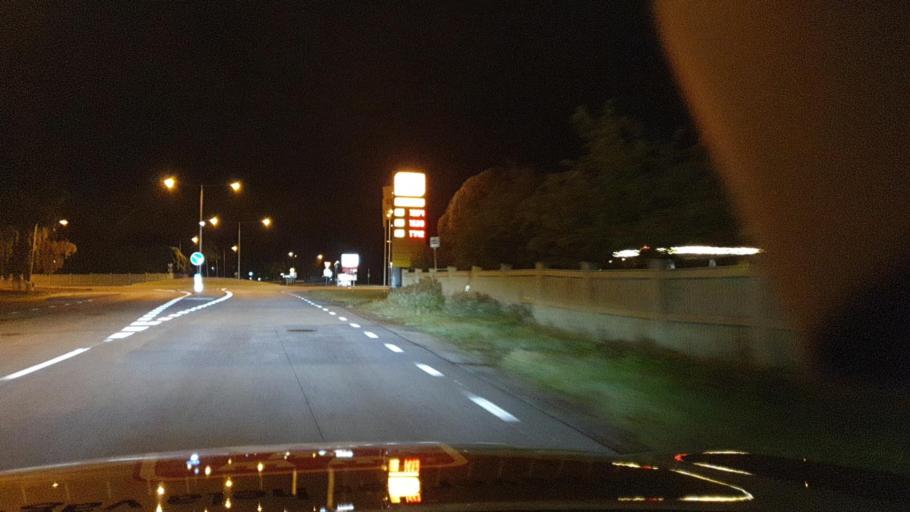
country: SE
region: Vaesternorrland
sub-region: Solleftea Kommun
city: Solleftea
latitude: 63.1776
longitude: 17.2775
